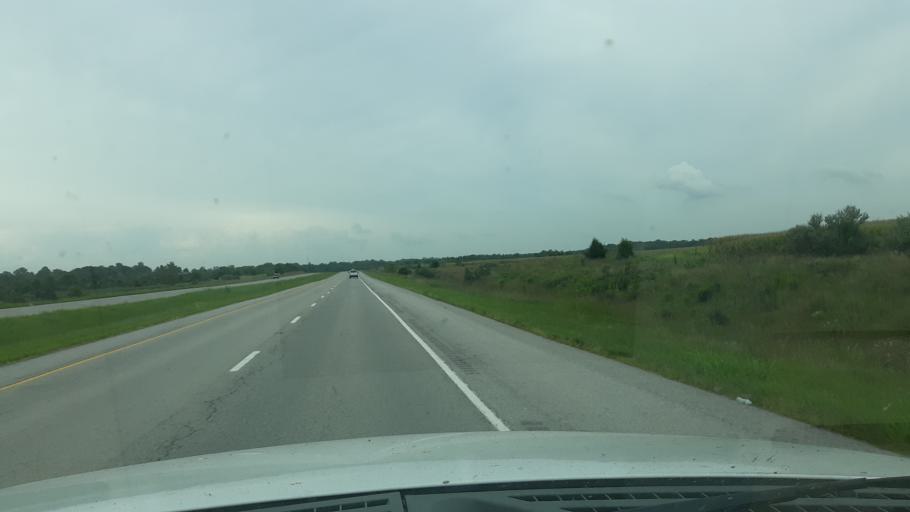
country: US
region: Illinois
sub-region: Saline County
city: Harrisburg
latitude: 37.7309
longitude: -88.5908
